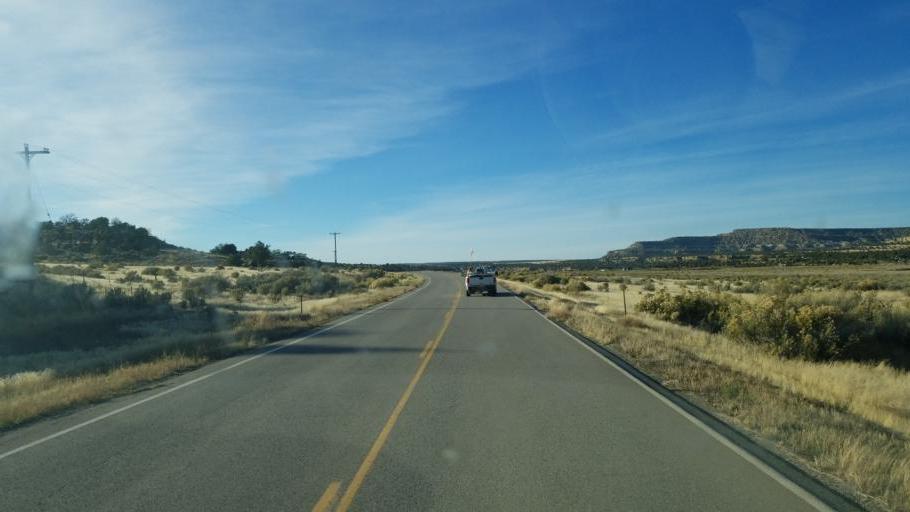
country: US
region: New Mexico
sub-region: San Juan County
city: Bloomfield
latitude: 36.7448
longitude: -107.5819
